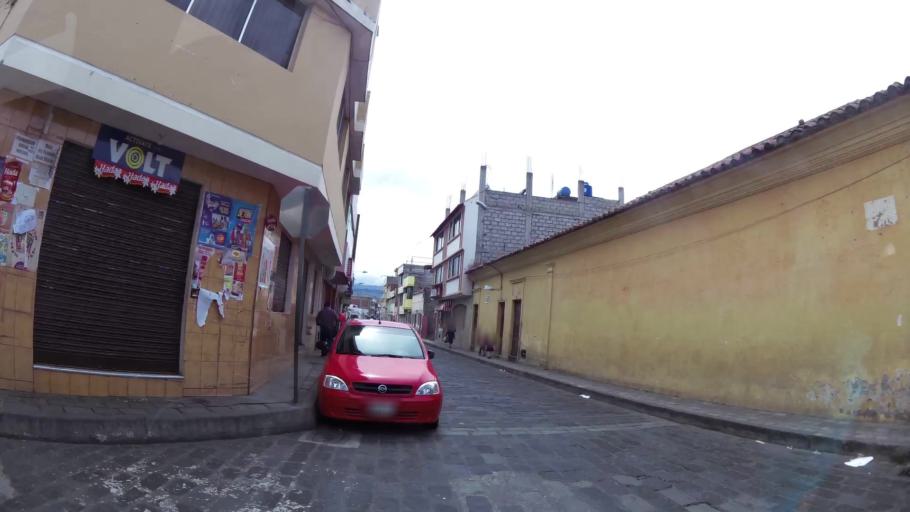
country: EC
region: Cotopaxi
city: Latacunga
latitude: -0.9292
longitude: -78.6137
